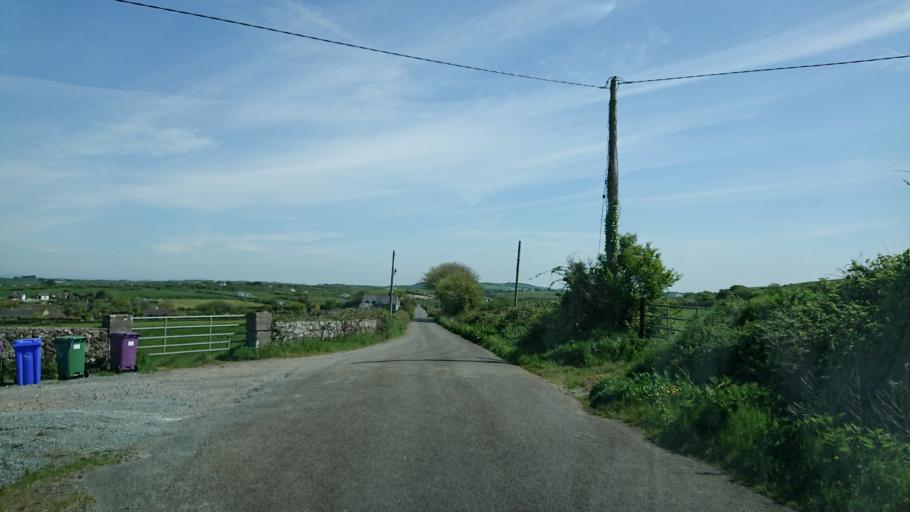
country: IE
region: Munster
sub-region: Waterford
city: Tra Mhor
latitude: 52.1540
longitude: -7.0725
